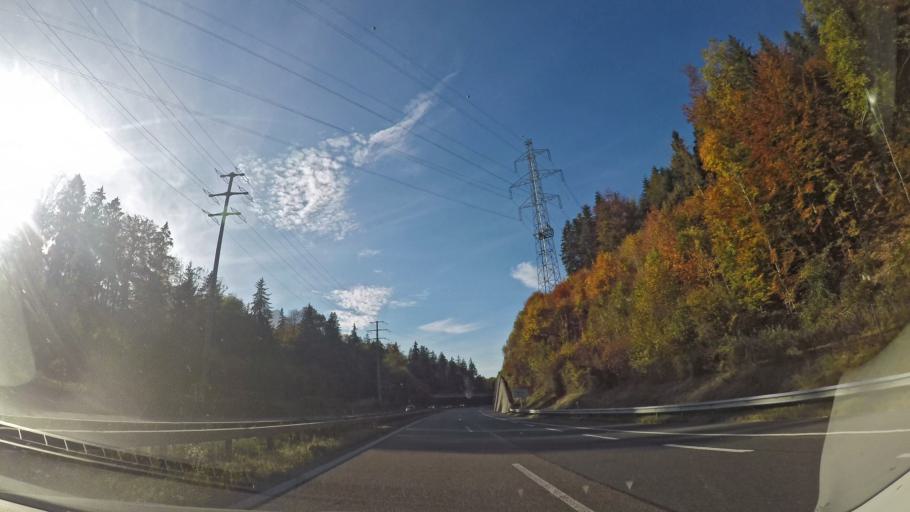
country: CH
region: Bern
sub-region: Frutigen-Niedersimmental District
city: Wimmis
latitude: 46.6947
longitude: 7.6462
